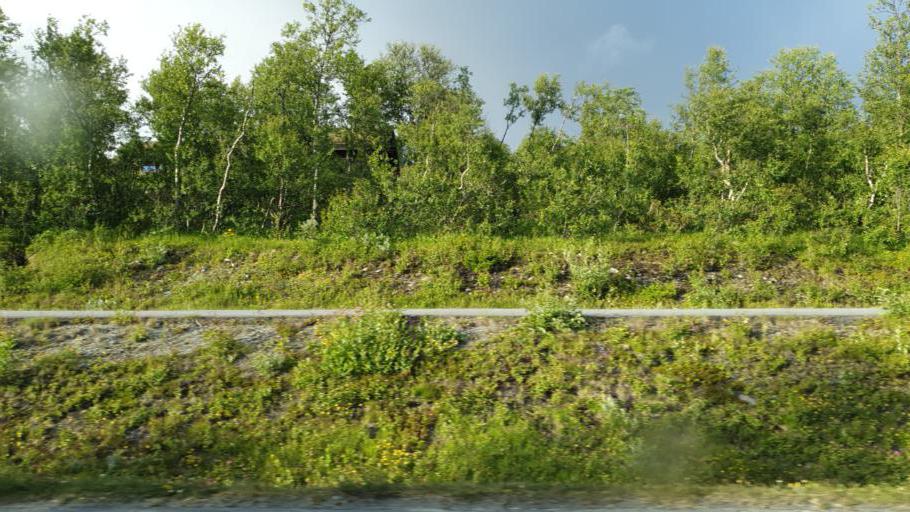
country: NO
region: Oppland
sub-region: Vestre Slidre
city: Slidre
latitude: 61.2537
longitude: 8.8795
